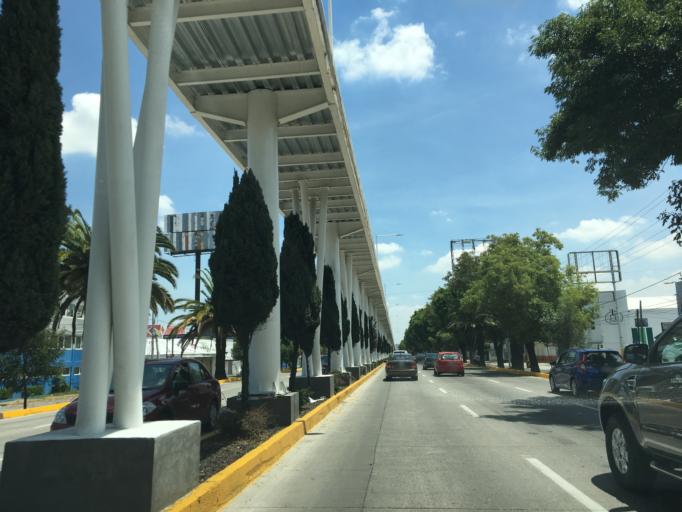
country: MX
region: Puebla
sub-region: Cuautlancingo
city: Sanctorum
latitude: 19.0828
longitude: -98.2286
